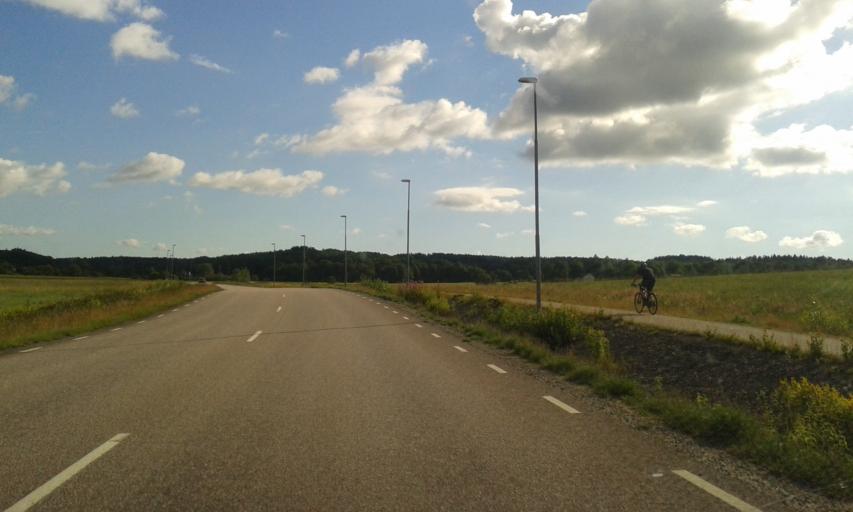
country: SE
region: Vaestra Goetaland
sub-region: Kungalvs Kommun
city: Diserod
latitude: 57.9194
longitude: 12.0243
